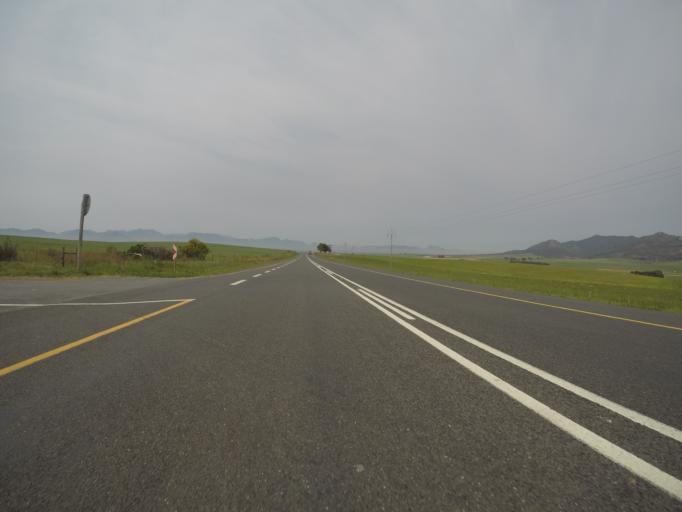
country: ZA
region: Western Cape
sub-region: West Coast District Municipality
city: Malmesbury
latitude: -33.5330
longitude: 18.8525
